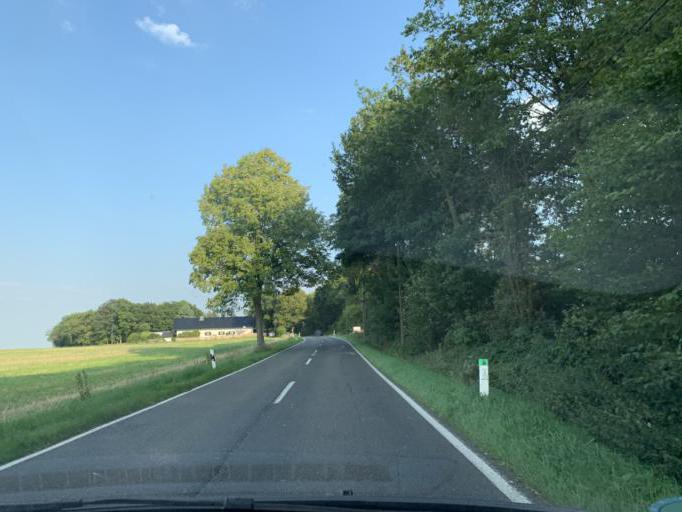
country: DE
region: North Rhine-Westphalia
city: Heimbach
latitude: 50.6535
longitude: 6.4378
